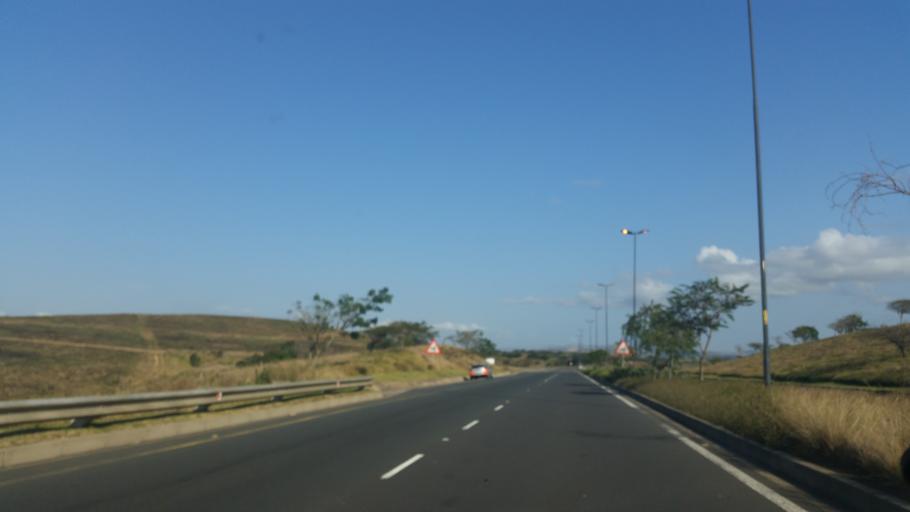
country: ZA
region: KwaZulu-Natal
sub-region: iLembe District Municipality
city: Ballitoville
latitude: -29.6271
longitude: 31.1114
